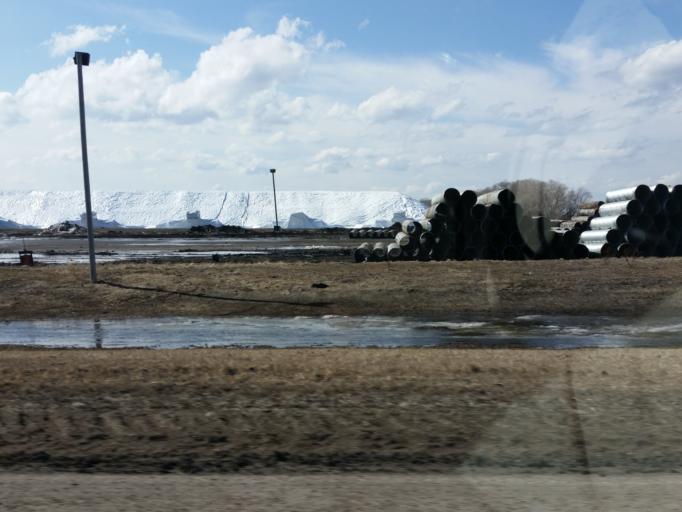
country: US
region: North Dakota
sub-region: Walsh County
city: Grafton
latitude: 48.2157
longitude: -97.3625
